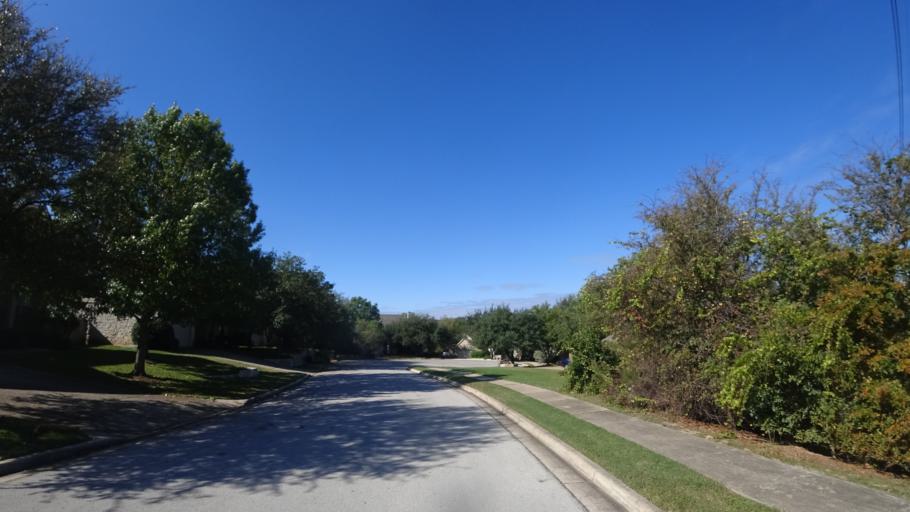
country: US
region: Texas
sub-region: Travis County
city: Hudson Bend
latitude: 30.3771
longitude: -97.8993
